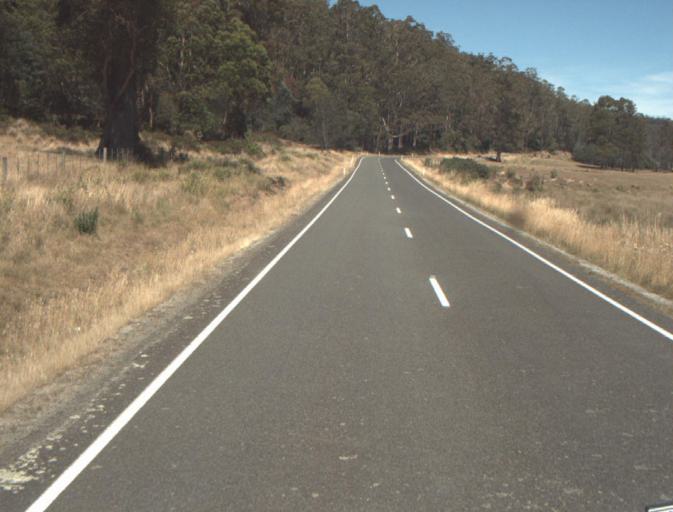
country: AU
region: Tasmania
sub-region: Dorset
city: Scottsdale
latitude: -41.2947
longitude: 147.3852
